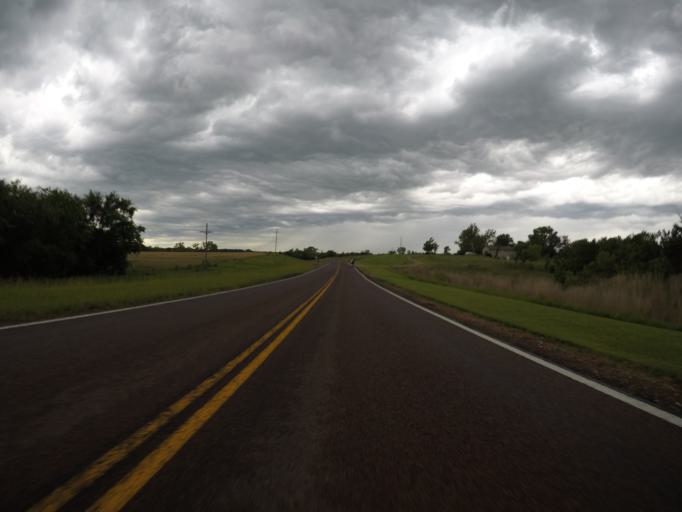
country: US
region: Kansas
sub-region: Shawnee County
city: Rossville
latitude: 38.9645
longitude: -96.0144
